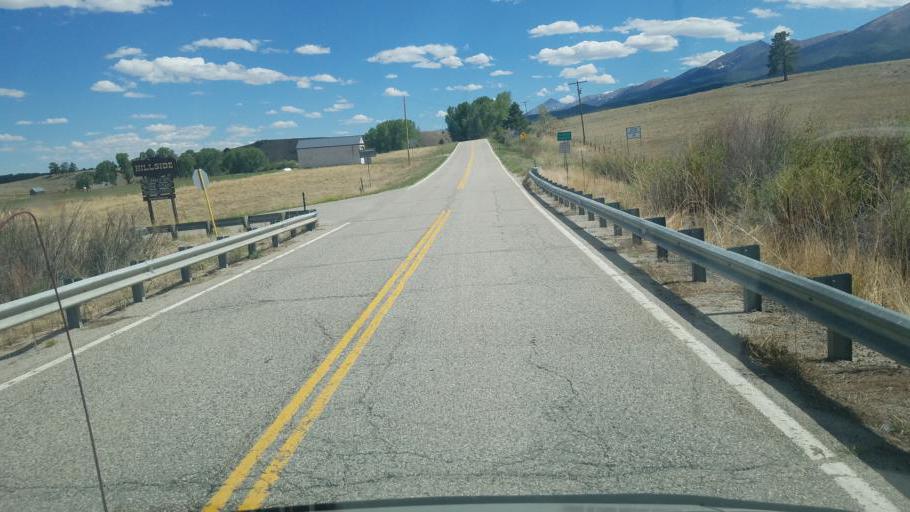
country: US
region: Colorado
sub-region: Custer County
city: Westcliffe
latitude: 38.2661
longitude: -105.6130
